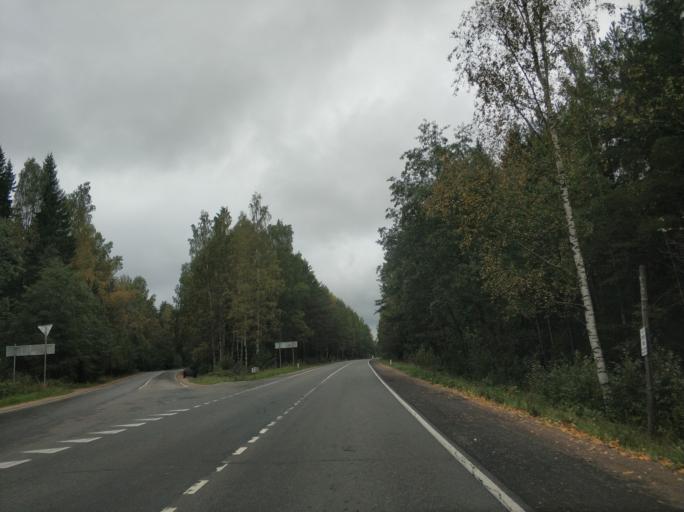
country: RU
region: Leningrad
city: Borisova Griva
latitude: 60.0900
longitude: 30.8618
